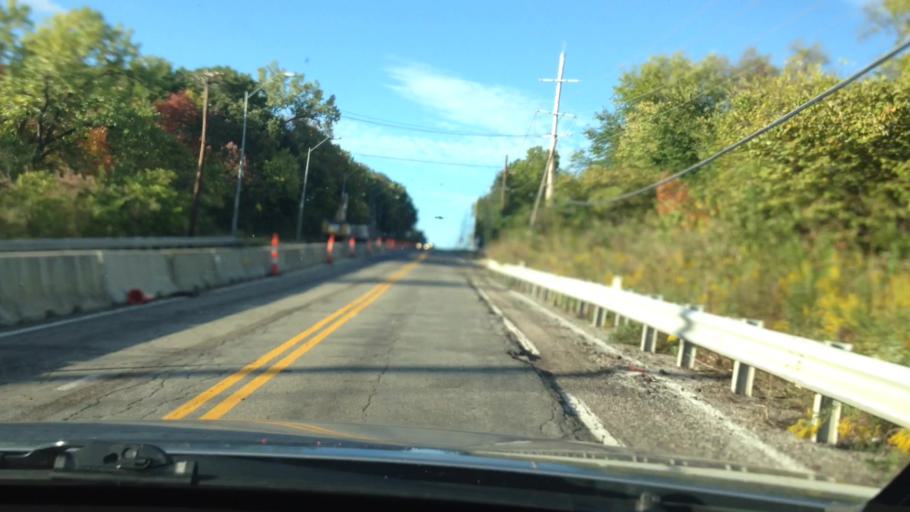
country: US
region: Missouri
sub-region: Clay County
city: North Kansas City
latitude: 39.1547
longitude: -94.5770
